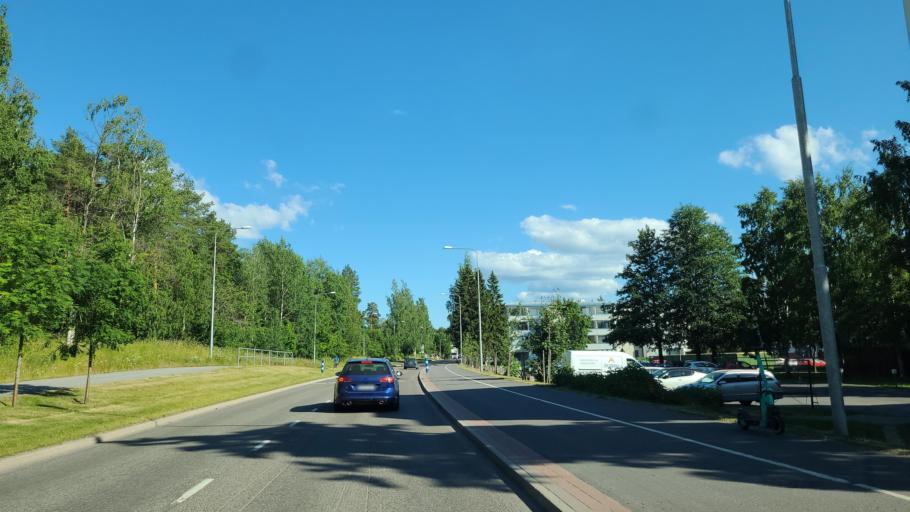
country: FI
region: Central Finland
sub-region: Jyvaeskylae
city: Jyvaeskylae
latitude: 62.2470
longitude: 25.7828
